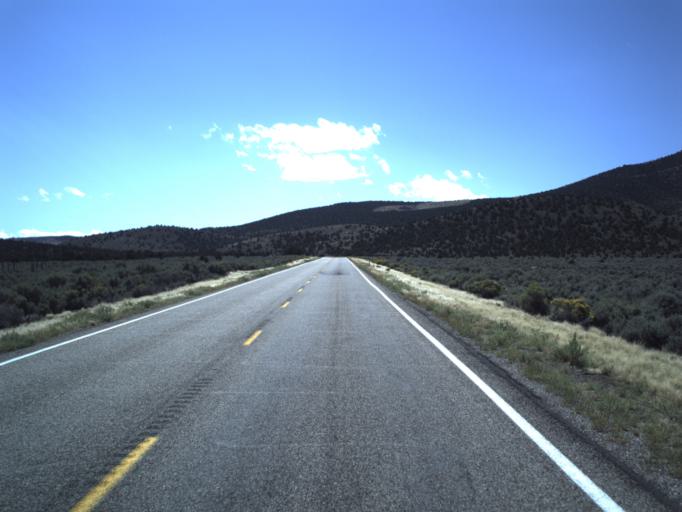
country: US
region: Utah
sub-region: Beaver County
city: Milford
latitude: 38.1393
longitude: -112.9601
